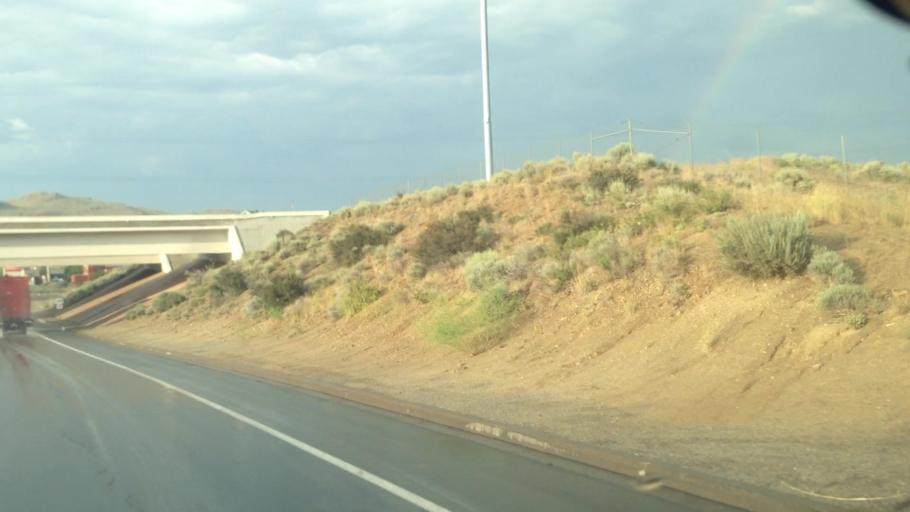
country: US
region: Nevada
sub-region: Washoe County
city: Golden Valley
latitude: 39.6103
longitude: -119.8515
